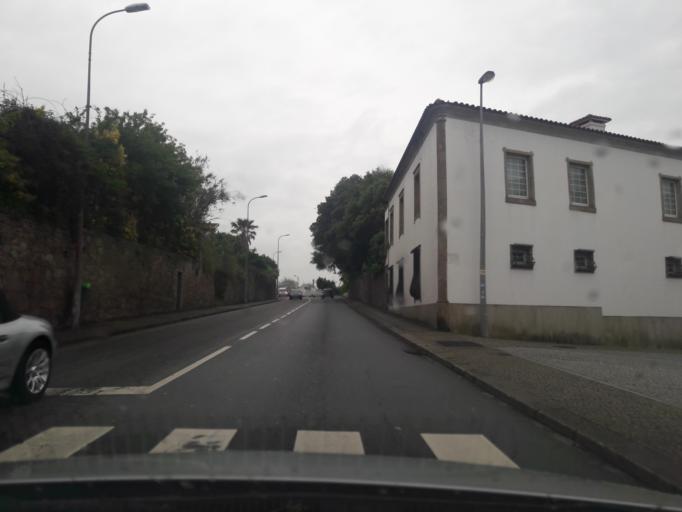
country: PT
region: Porto
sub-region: Vila do Conde
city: Vila do Conde
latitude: 41.3468
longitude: -8.7382
